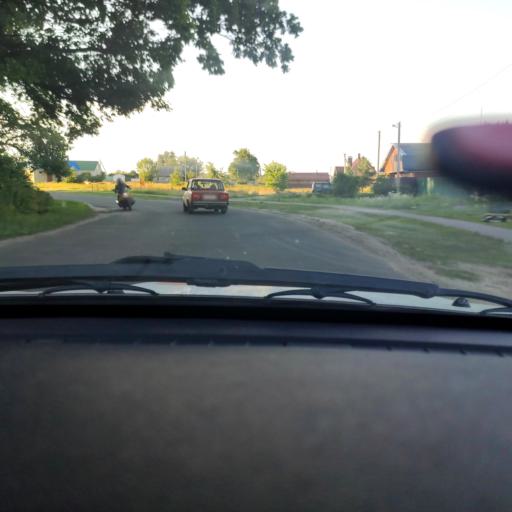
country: RU
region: Voronezj
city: Ramon'
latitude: 51.8999
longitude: 39.2867
